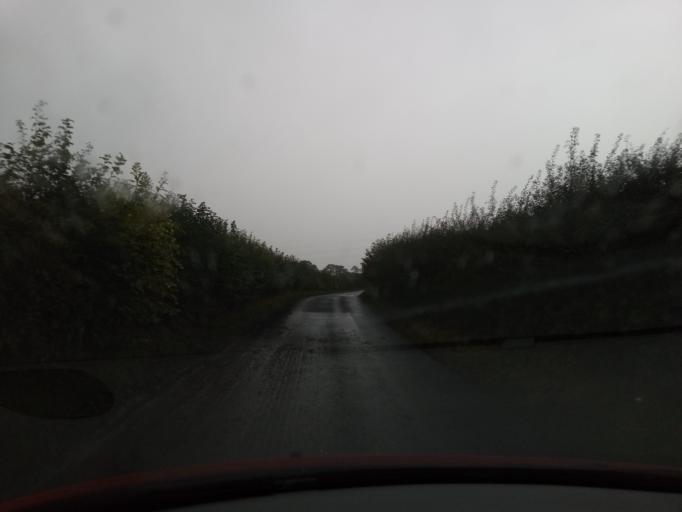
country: GB
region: Scotland
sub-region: The Scottish Borders
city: Selkirk
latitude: 55.5073
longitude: -2.7939
